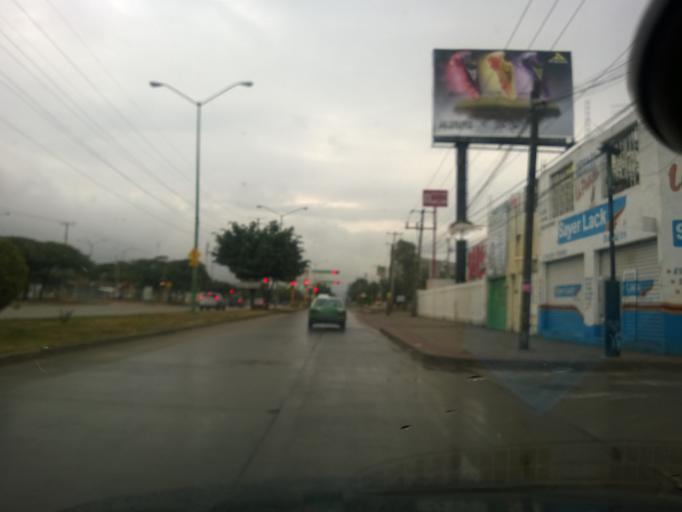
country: MX
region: Guanajuato
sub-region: Leon
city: Medina
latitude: 21.1445
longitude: -101.6456
